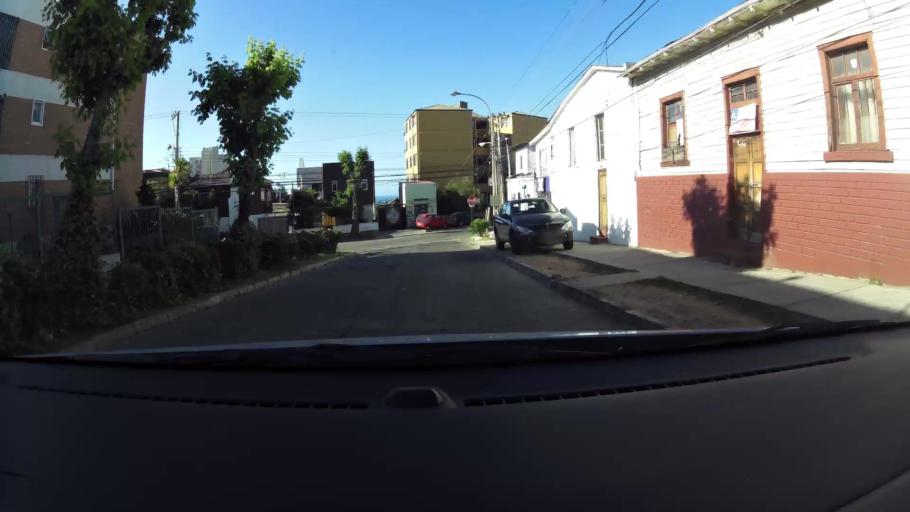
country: CL
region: Valparaiso
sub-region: Provincia de Valparaiso
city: Vina del Mar
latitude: -33.0266
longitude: -71.5686
